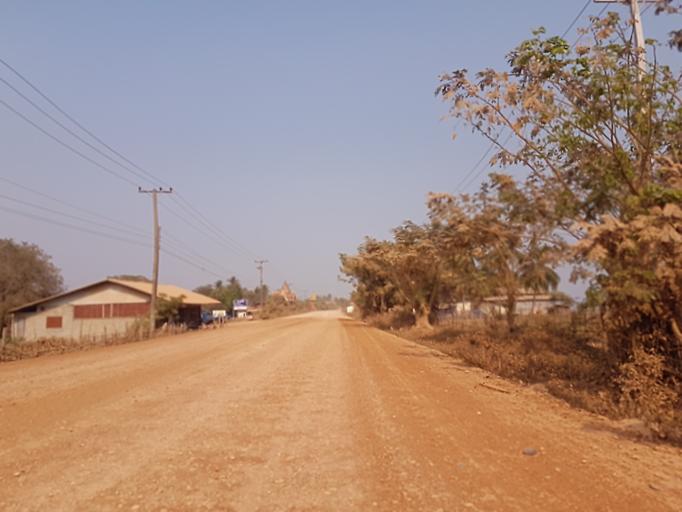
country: TH
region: Nong Khai
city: Nong Khai
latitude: 17.9401
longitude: 102.7923
